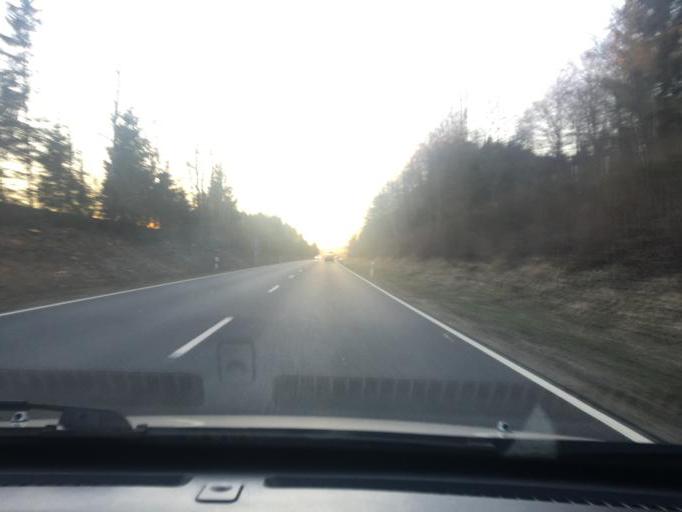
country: DE
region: Baden-Wuerttemberg
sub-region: Tuebingen Region
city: Berkheim
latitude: 48.0500
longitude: 10.0717
